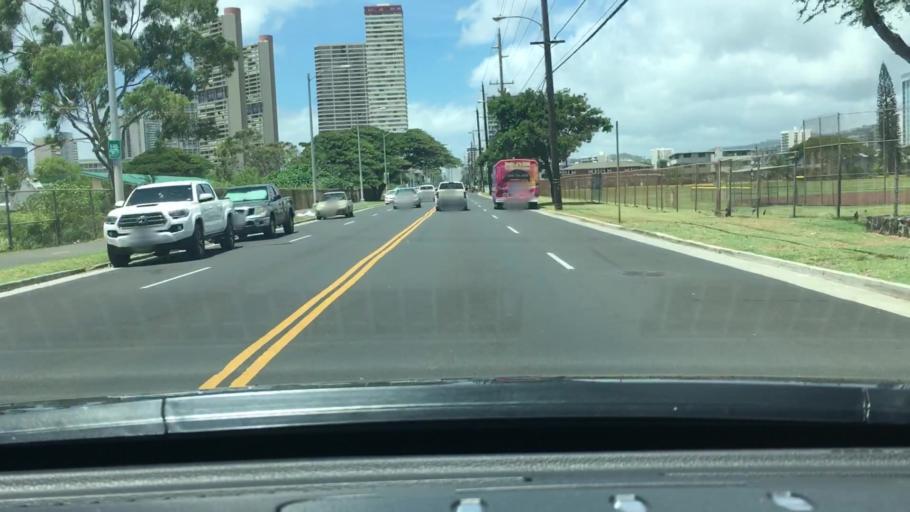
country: US
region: Hawaii
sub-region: Honolulu County
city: Honolulu
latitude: 21.2835
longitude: -157.8190
